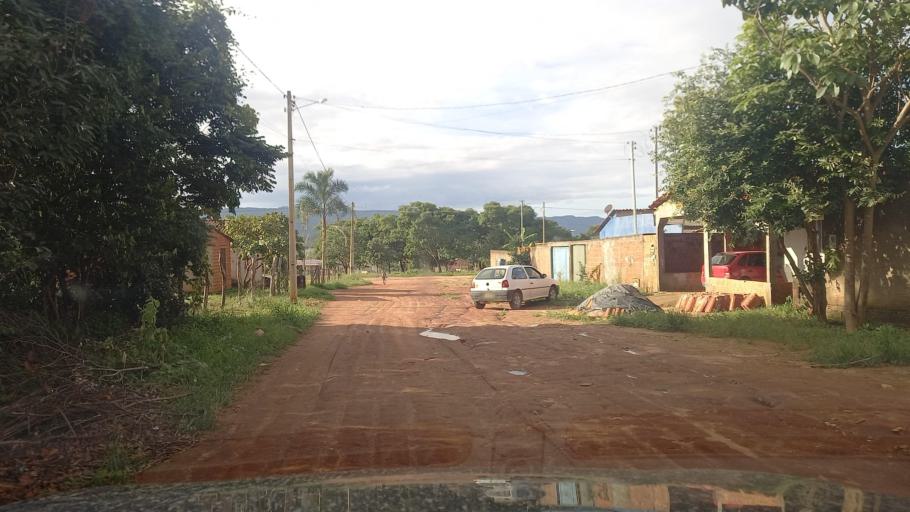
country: BR
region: Goias
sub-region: Cavalcante
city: Cavalcante
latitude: -13.7978
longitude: -47.4403
